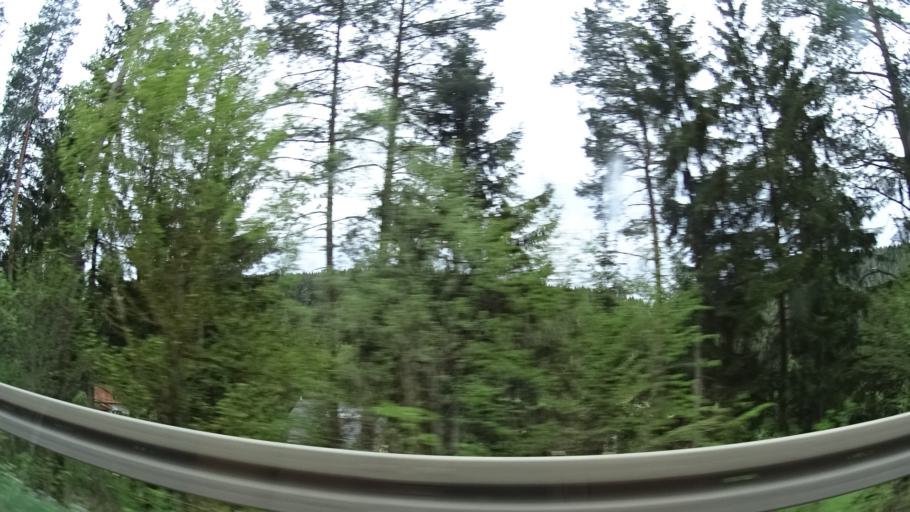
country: DE
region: Baden-Wuerttemberg
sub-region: Freiburg Region
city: Niedereschach
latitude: 48.1417
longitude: 8.5363
